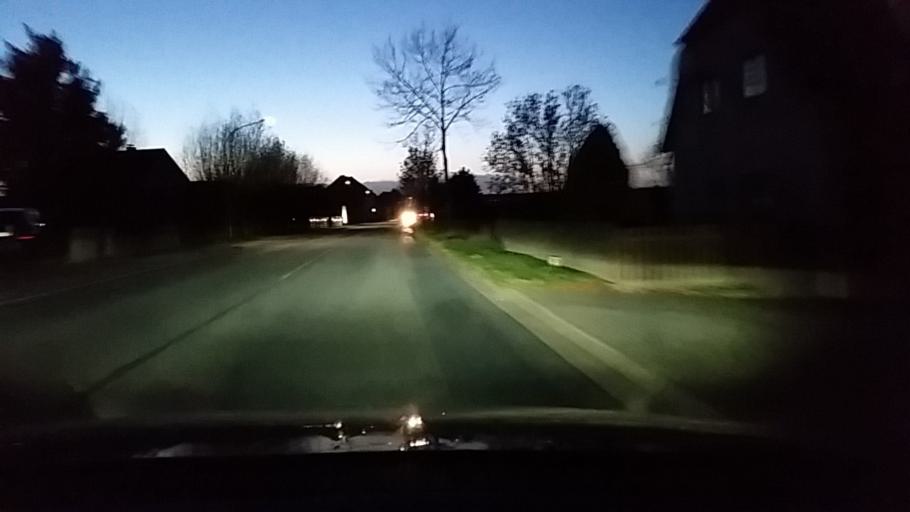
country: DE
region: Lower Saxony
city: Calberlah
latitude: 52.3939
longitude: 10.6327
